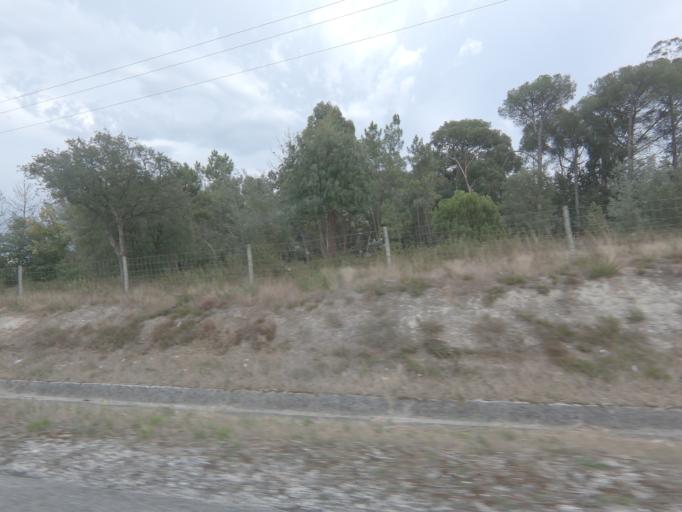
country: PT
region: Viseu
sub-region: Santa Comba Dao
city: Santa Comba Dao
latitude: 40.3636
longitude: -8.1334
